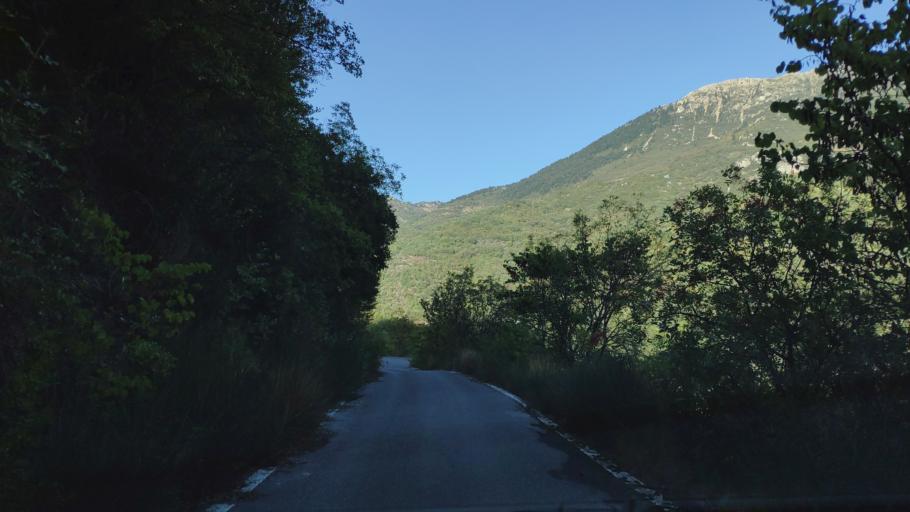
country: GR
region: Peloponnese
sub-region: Nomos Arkadias
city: Dimitsana
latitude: 37.5588
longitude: 22.0430
